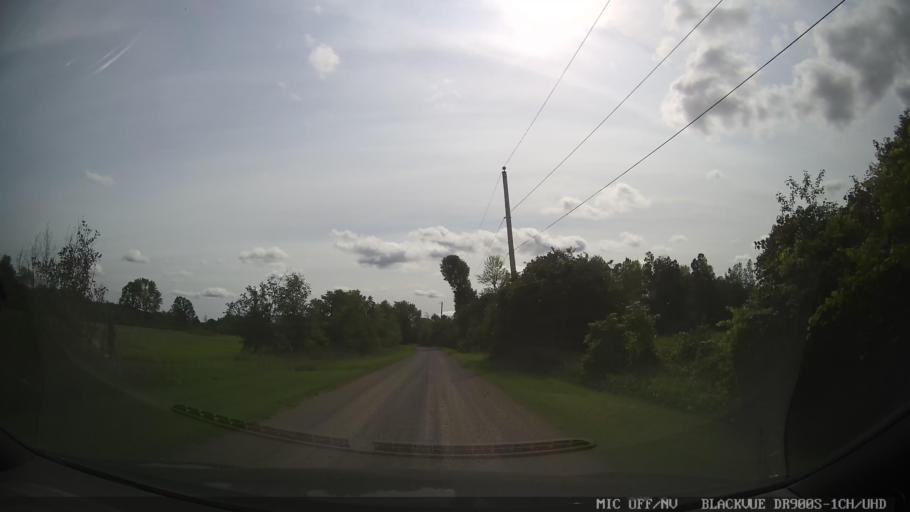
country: CA
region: Ontario
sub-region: Lanark County
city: Smiths Falls
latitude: 44.9179
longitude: -75.9277
